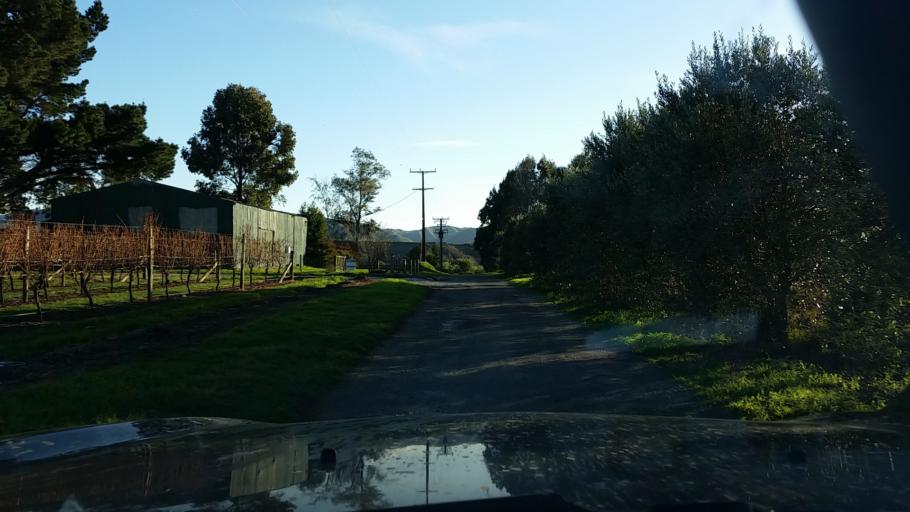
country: NZ
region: Marlborough
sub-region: Marlborough District
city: Blenheim
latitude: -41.6667
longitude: 174.0664
